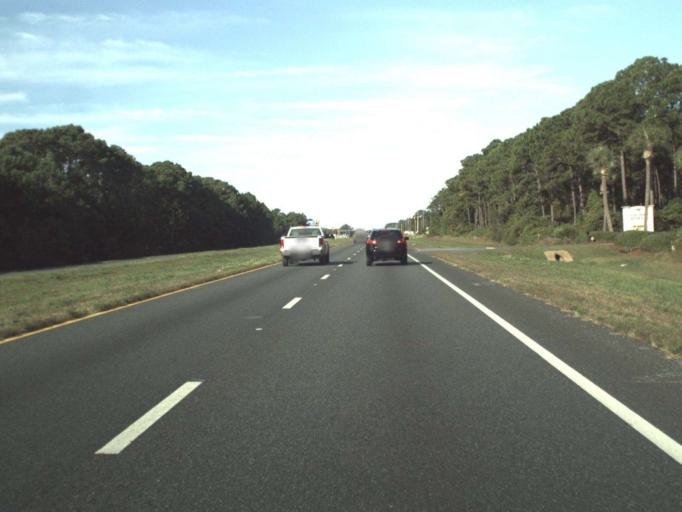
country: US
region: Florida
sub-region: Walton County
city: Miramar Beach
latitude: 30.3850
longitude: -86.3711
